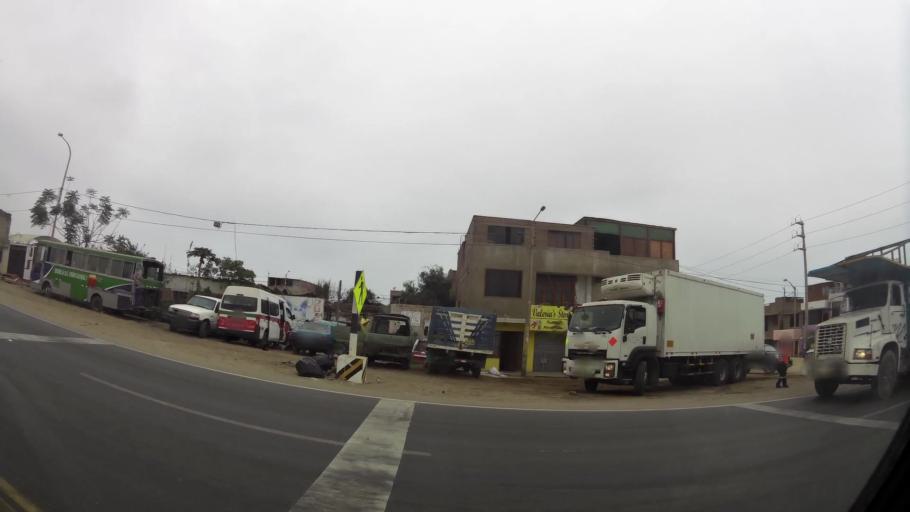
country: PE
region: La Libertad
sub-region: Provincia de Trujillo
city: Moche
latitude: -8.1778
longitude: -78.9933
